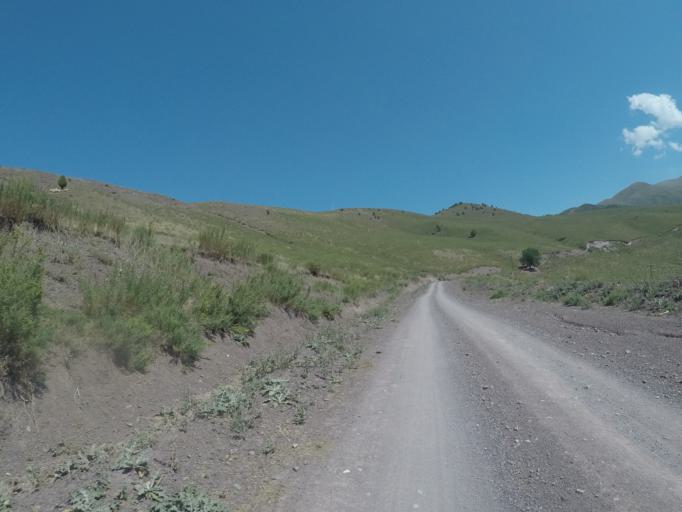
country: KG
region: Chuy
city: Bishkek
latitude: 42.6513
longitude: 74.5178
